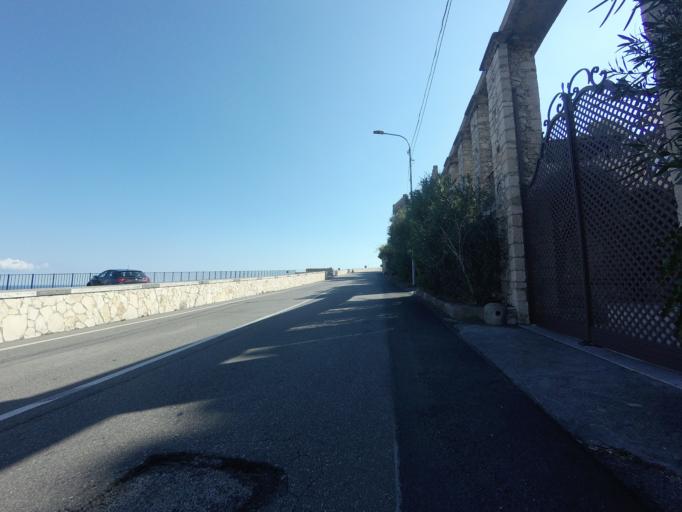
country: IT
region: Sicily
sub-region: Messina
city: Taormina
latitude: 37.8478
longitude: 15.2969
